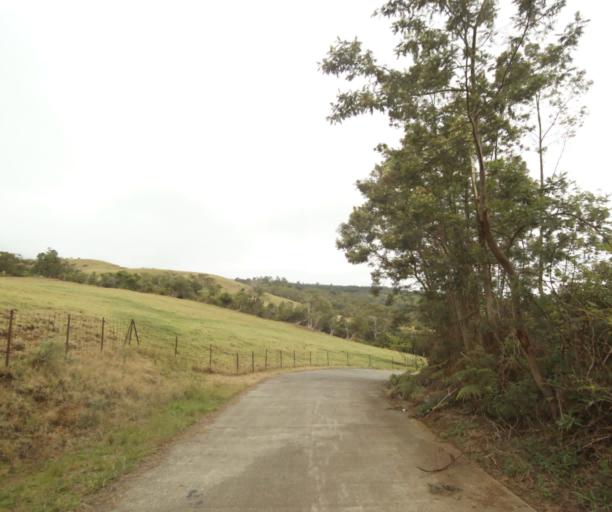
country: RE
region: Reunion
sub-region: Reunion
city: Saint-Paul
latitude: -21.0177
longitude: 55.3534
